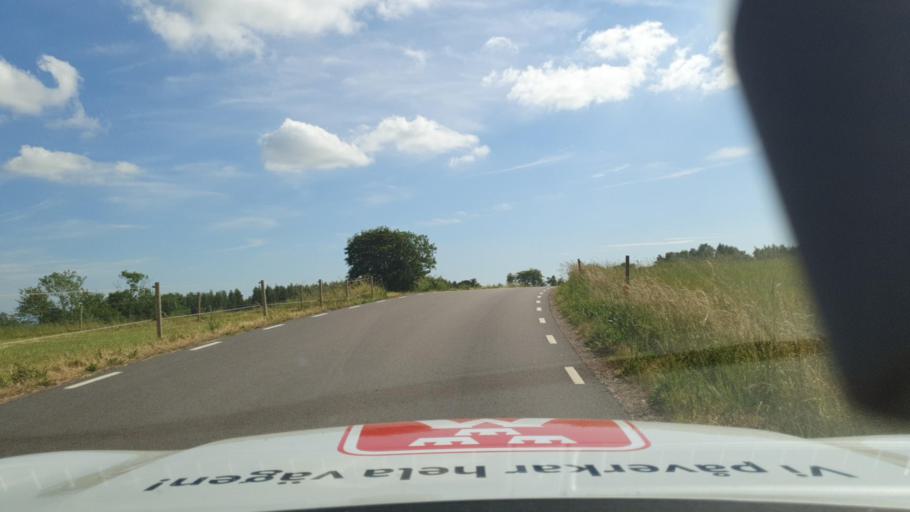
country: SE
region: Skane
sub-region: Sjobo Kommun
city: Blentarp
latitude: 55.5431
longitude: 13.5597
